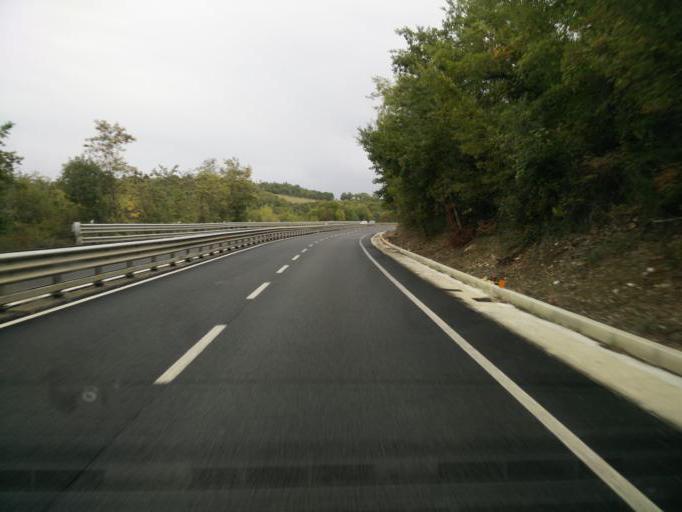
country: IT
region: Tuscany
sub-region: Province of Florence
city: Barberino Val d'Elsa
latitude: 43.5295
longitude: 11.2096
